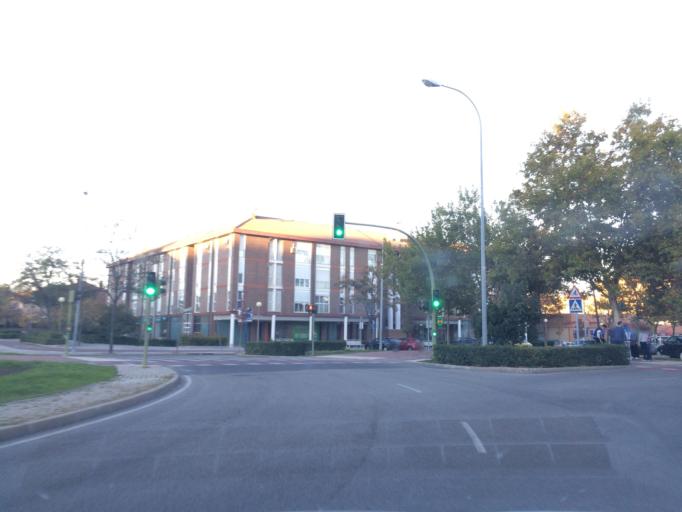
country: ES
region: Madrid
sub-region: Provincia de Madrid
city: Tres Cantos
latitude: 40.5953
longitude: -3.7065
